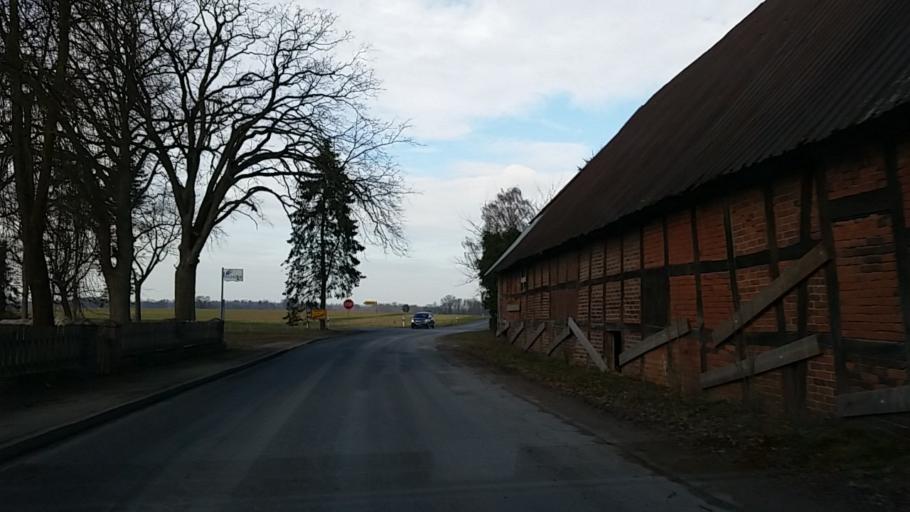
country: DE
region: Lower Saxony
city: Altenmedingen
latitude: 53.1363
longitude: 10.6350
